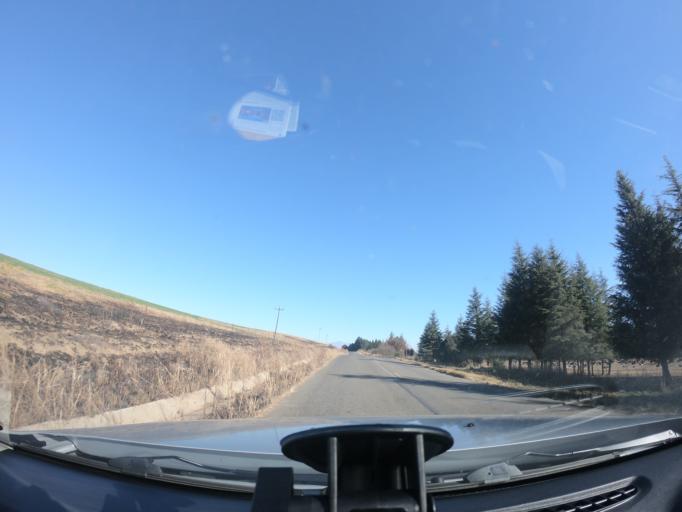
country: ZA
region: KwaZulu-Natal
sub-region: uMgungundlovu District Municipality
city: Mooirivier
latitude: -29.3257
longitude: 29.8586
